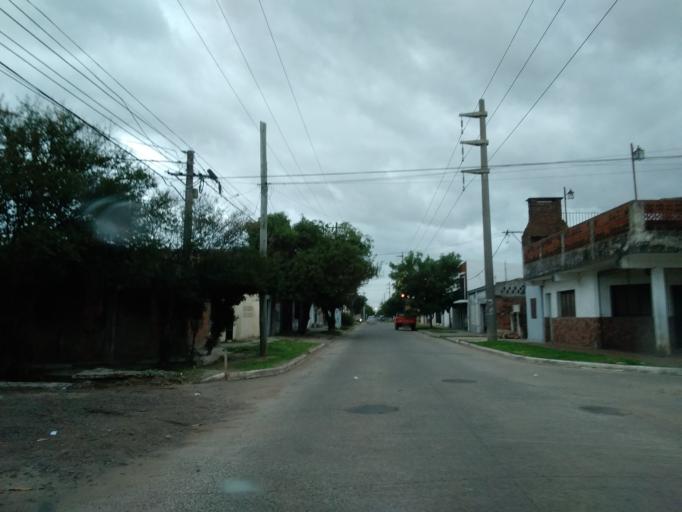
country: AR
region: Corrientes
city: Corrientes
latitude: -27.4800
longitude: -58.8216
